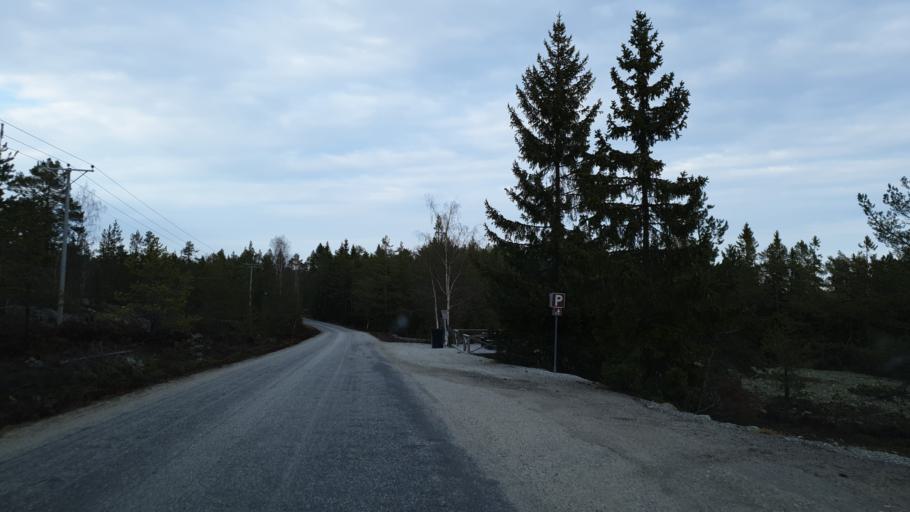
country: SE
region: Vaesternorrland
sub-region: Sundsvalls Kommun
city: Njurundabommen
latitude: 61.9685
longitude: 17.3808
